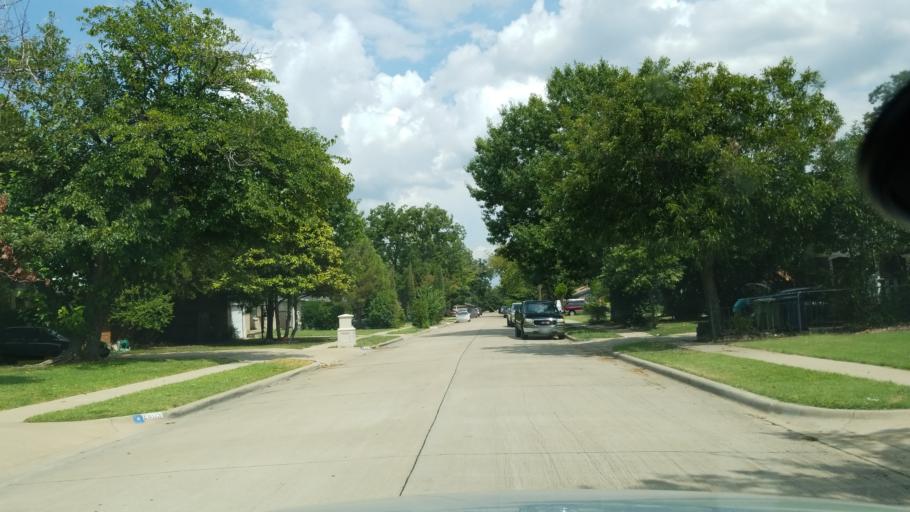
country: US
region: Texas
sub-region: Dallas County
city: Garland
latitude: 32.9193
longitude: -96.6676
